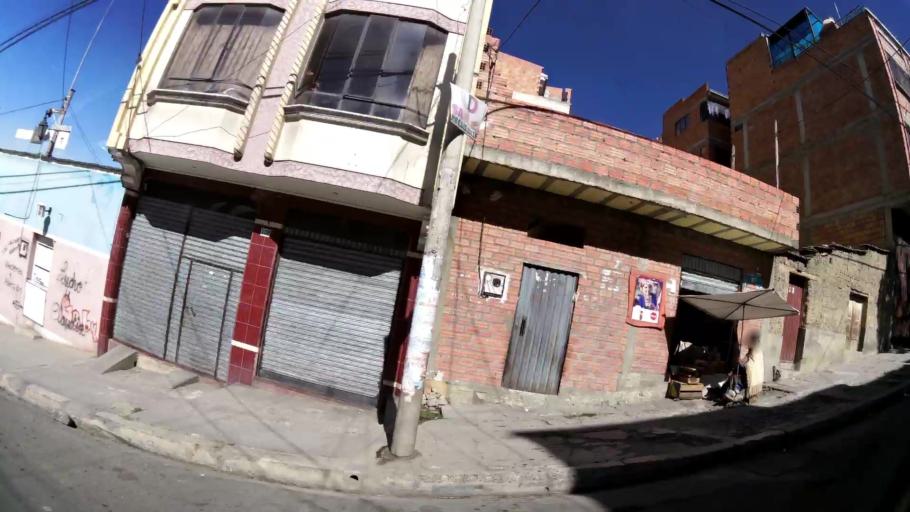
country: BO
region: La Paz
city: La Paz
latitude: -16.5051
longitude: -68.1468
